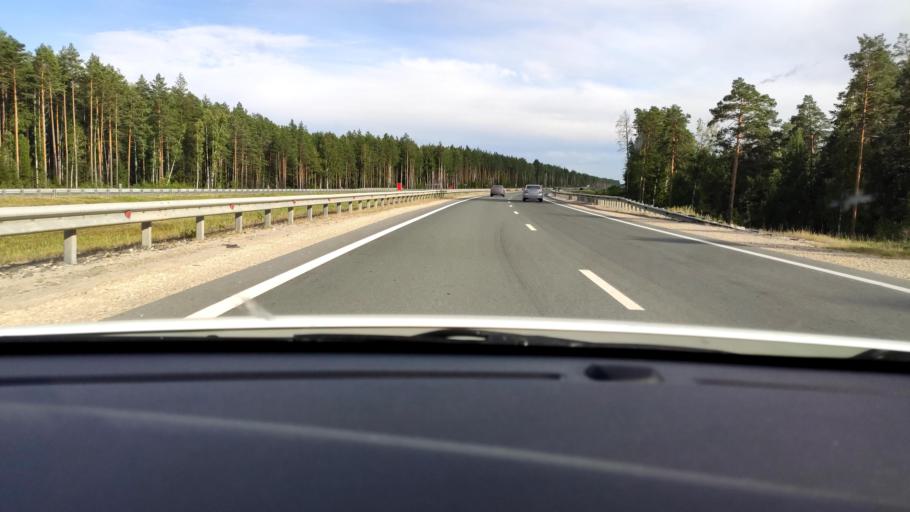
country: RU
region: Mariy-El
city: Surok
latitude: 56.5324
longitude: 47.9991
